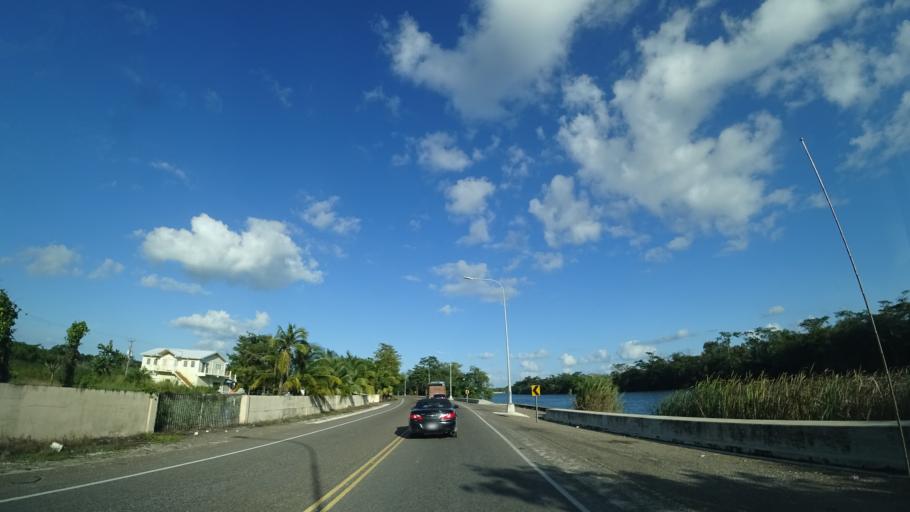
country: BZ
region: Belize
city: Belize City
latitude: 17.5453
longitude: -88.2819
